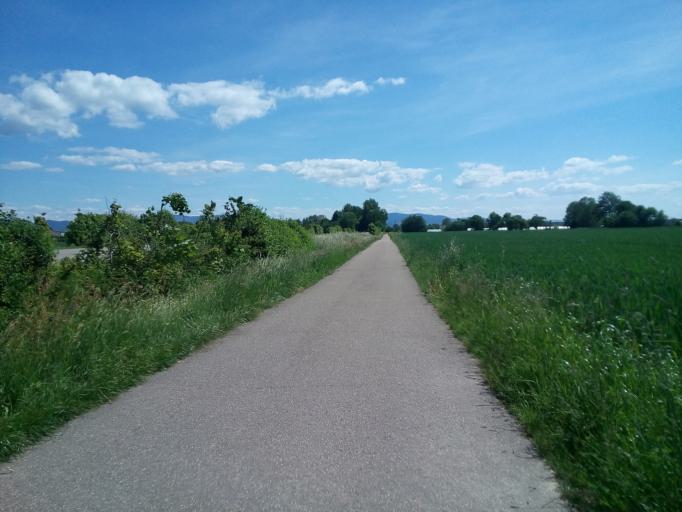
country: DE
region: Baden-Wuerttemberg
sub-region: Freiburg Region
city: Renchen
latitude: 48.6077
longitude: 8.0050
